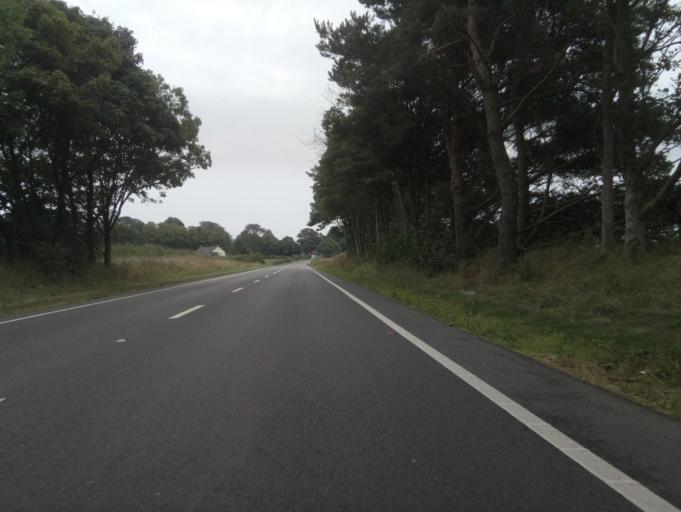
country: GB
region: Scotland
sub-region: Dumfries and Galloway
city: Locharbriggs
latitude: 55.0656
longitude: -3.5092
